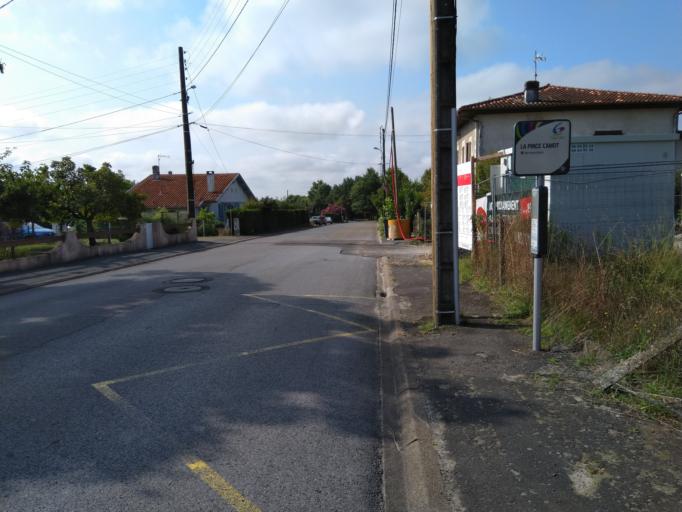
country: FR
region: Aquitaine
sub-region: Departement des Landes
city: Saint-Paul-les-Dax
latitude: 43.7267
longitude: -1.0837
